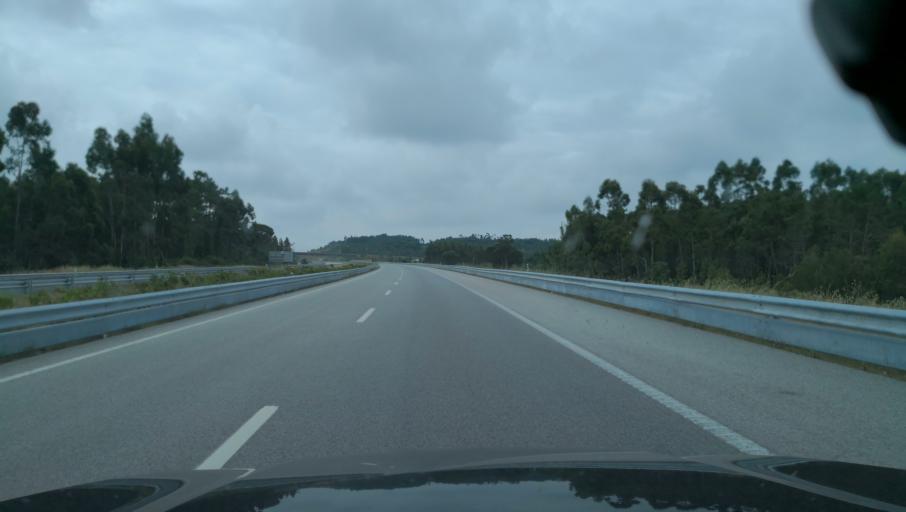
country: PT
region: Coimbra
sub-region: Figueira da Foz
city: Alhadas
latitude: 40.1976
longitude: -8.8146
